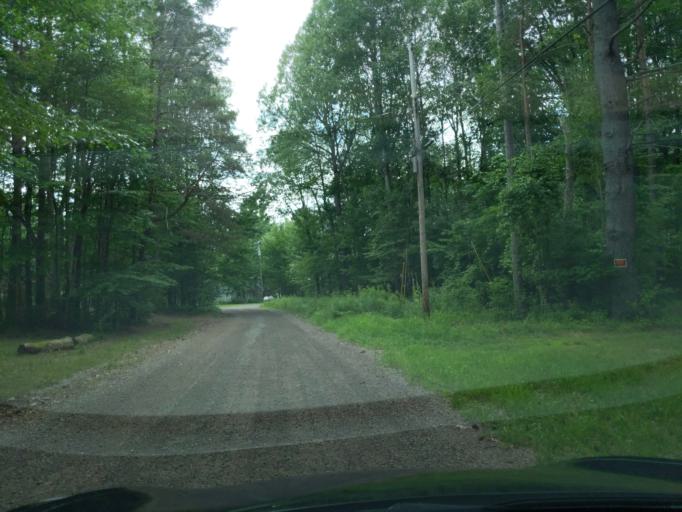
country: US
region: Michigan
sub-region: Clare County
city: Harrison
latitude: 43.9781
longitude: -85.0027
